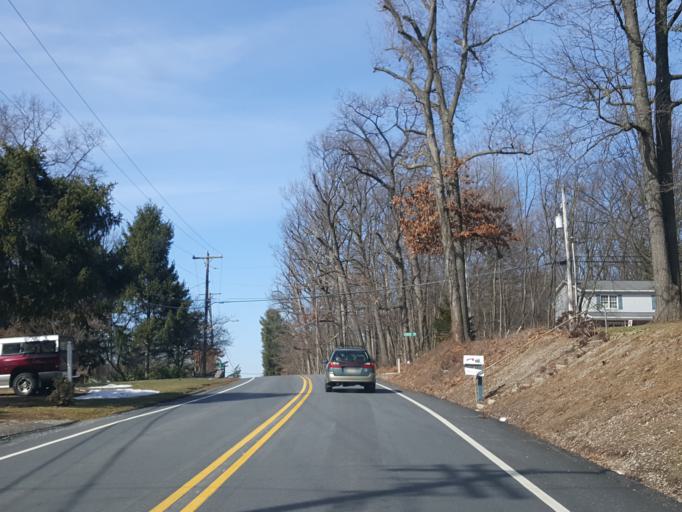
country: US
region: Pennsylvania
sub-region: Lebanon County
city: Campbelltown
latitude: 40.2571
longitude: -76.5512
